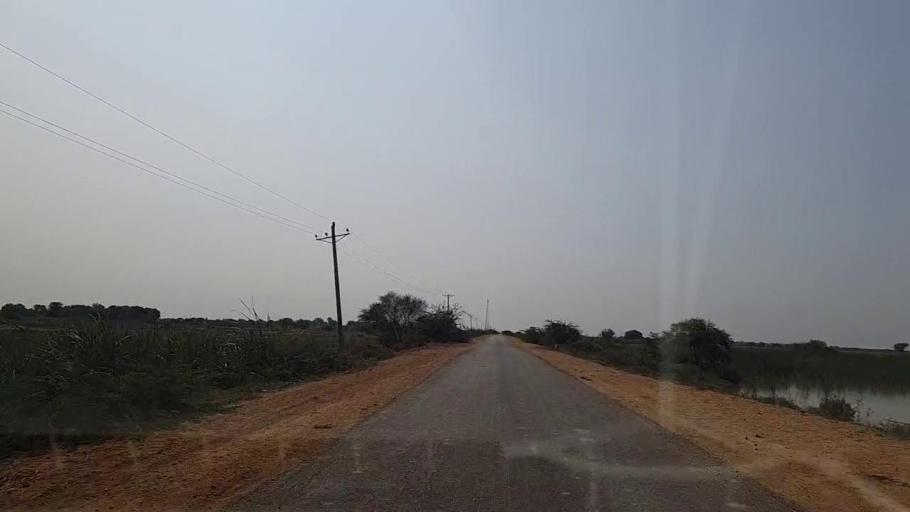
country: PK
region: Sindh
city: Chuhar Jamali
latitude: 24.2929
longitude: 67.9278
